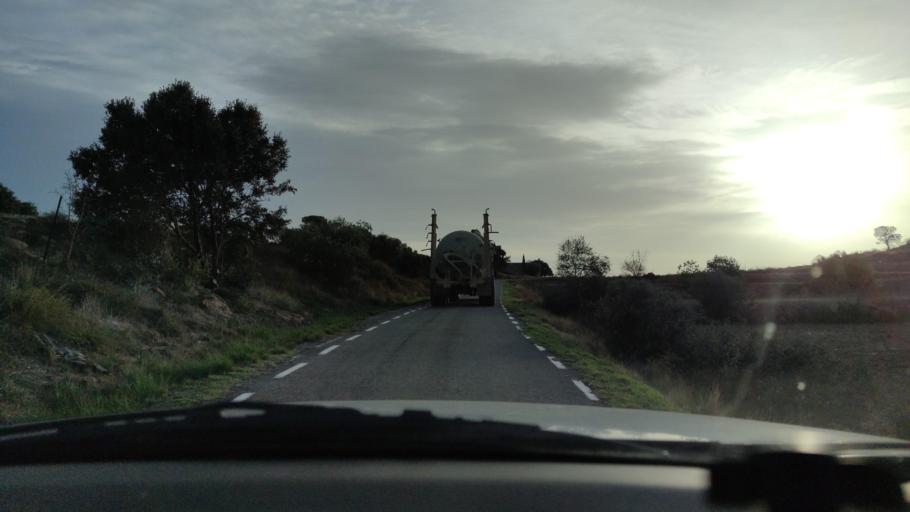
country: ES
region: Catalonia
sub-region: Provincia de Lleida
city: Agramunt
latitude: 41.8376
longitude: 1.0933
